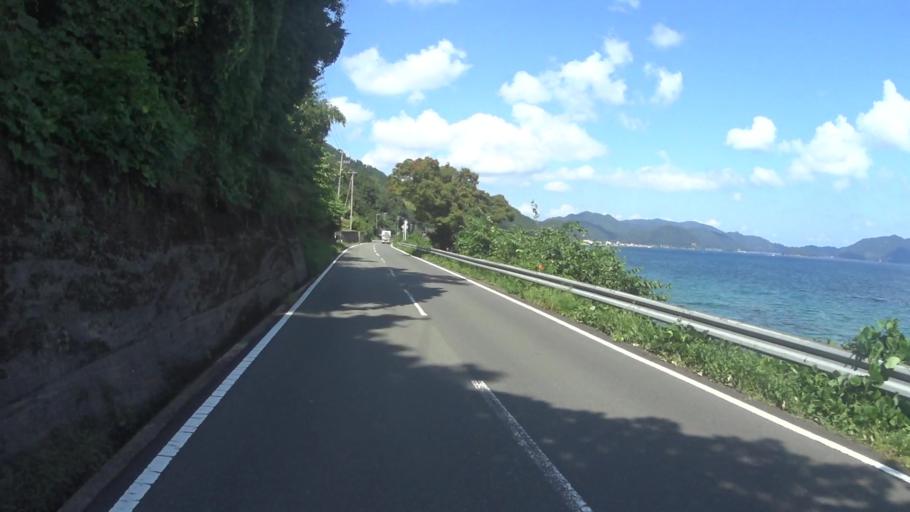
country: JP
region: Kyoto
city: Miyazu
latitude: 35.6409
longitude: 135.2504
